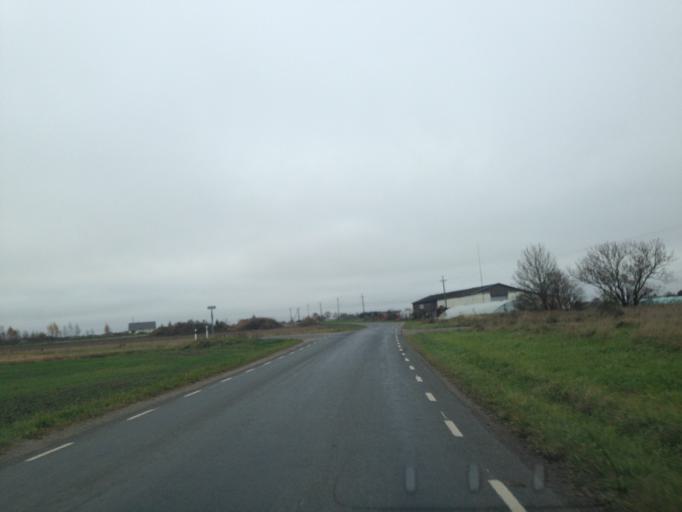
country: EE
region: Harju
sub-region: Saue linn
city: Saue
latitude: 59.3527
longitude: 24.5580
